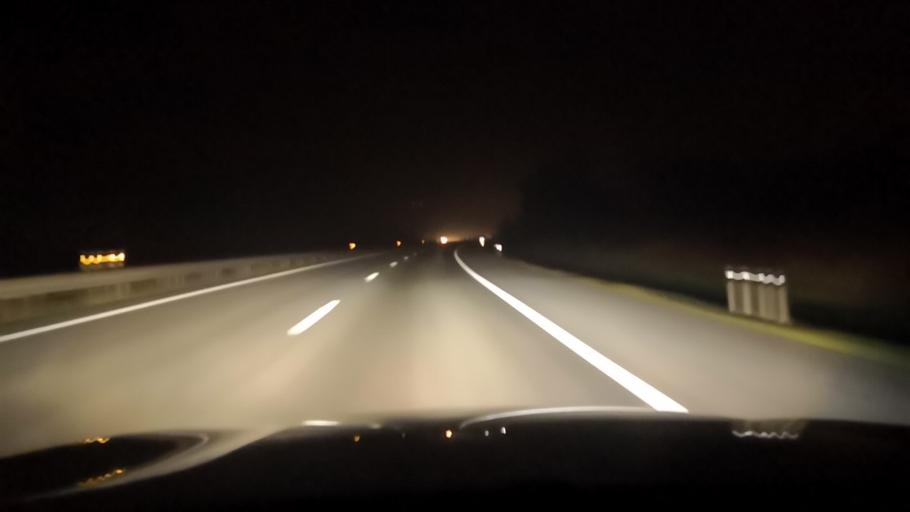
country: PT
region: Santarem
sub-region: Benavente
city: Benavente
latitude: 38.9429
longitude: -8.8194
